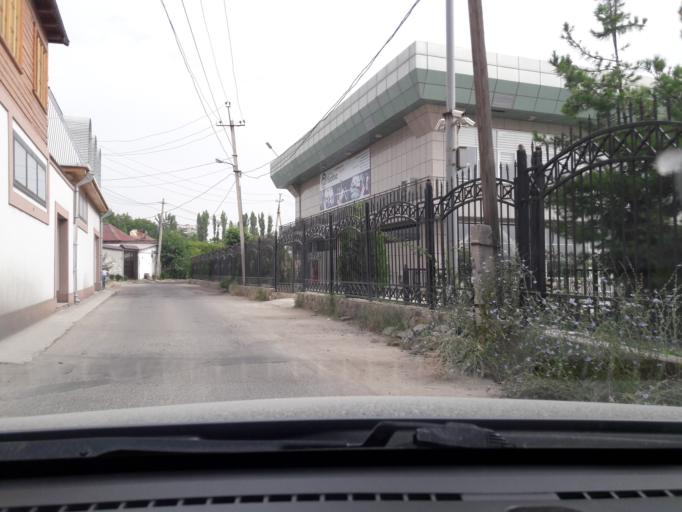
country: TJ
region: Dushanbe
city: Dushanbe
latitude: 38.5798
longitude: 68.7646
